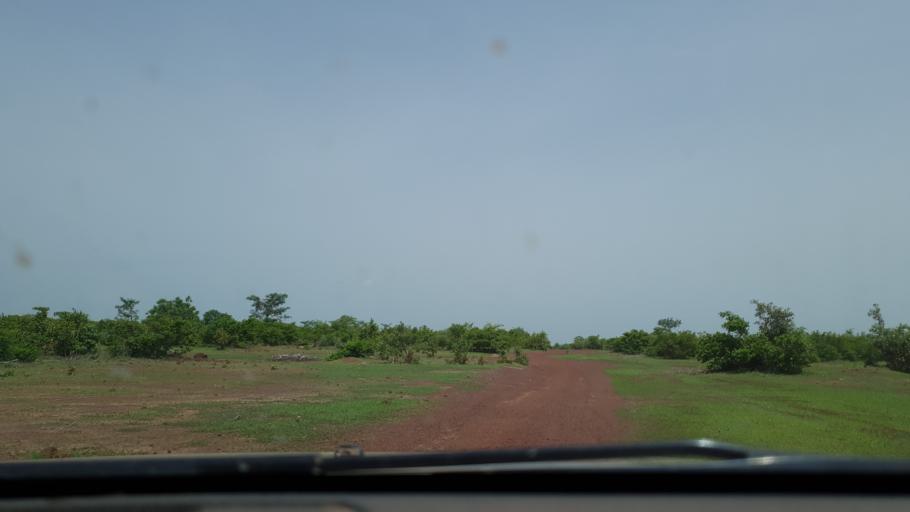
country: ML
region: Koulikoro
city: Koulikoro
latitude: 12.6657
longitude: -7.2288
